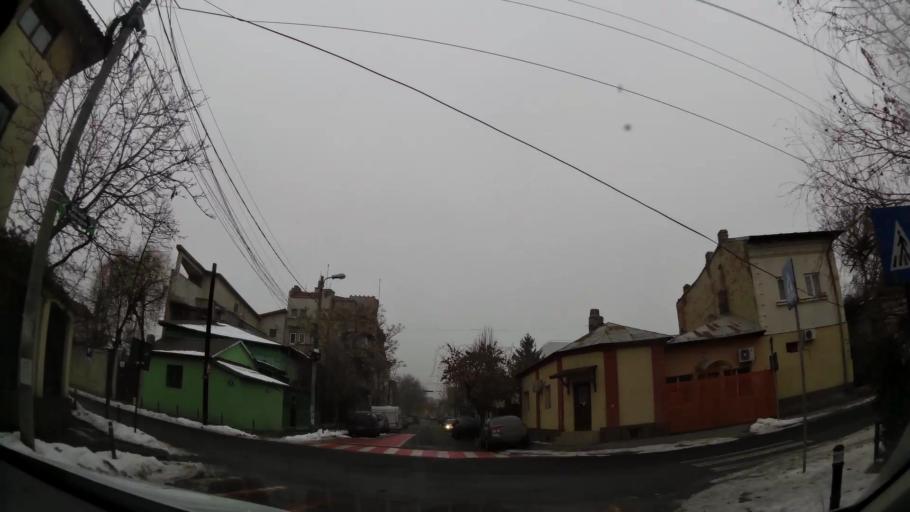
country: RO
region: Bucuresti
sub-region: Municipiul Bucuresti
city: Bucharest
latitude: 44.4355
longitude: 26.1293
